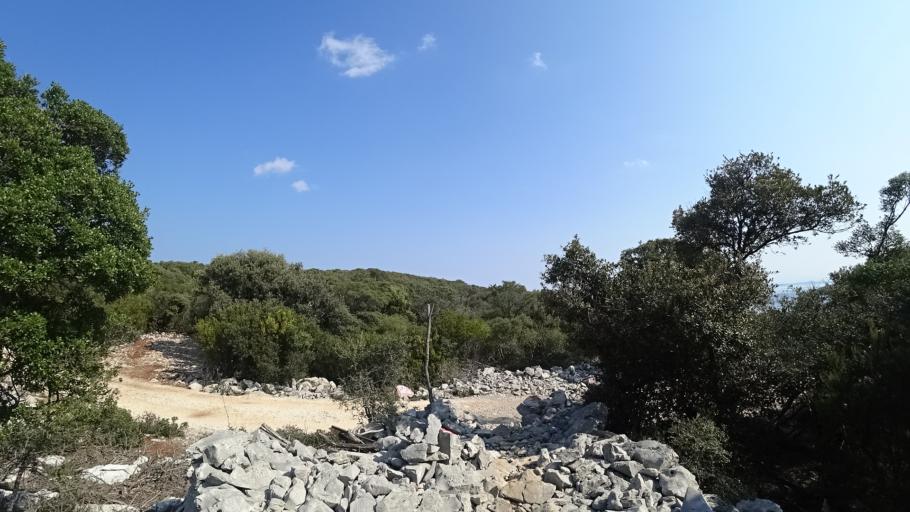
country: HR
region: Primorsko-Goranska
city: Mali Losinj
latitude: 44.4877
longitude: 14.5355
